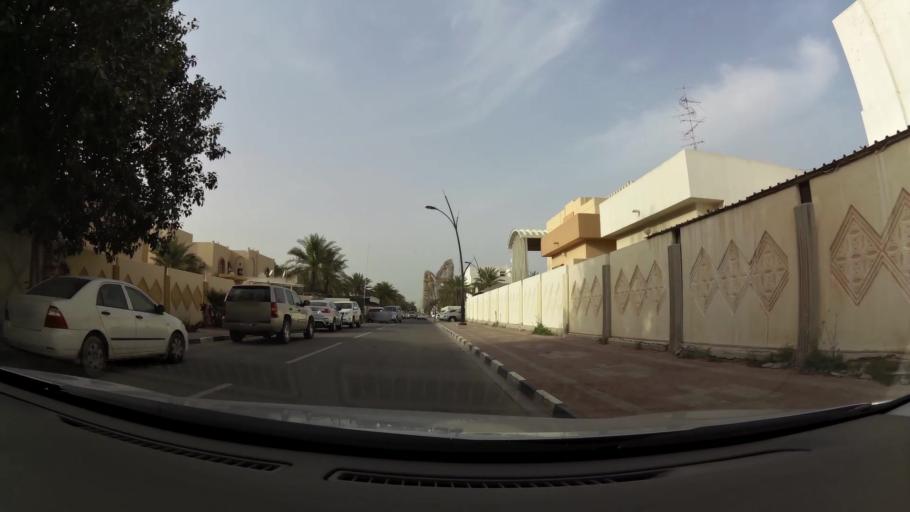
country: QA
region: Baladiyat ad Dawhah
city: Doha
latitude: 25.3281
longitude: 51.5176
